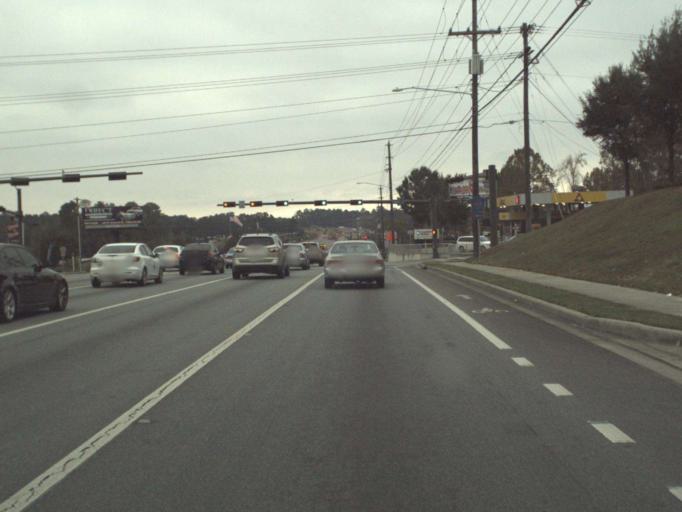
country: US
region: Florida
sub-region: Leon County
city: Tallahassee
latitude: 30.4641
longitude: -84.3614
